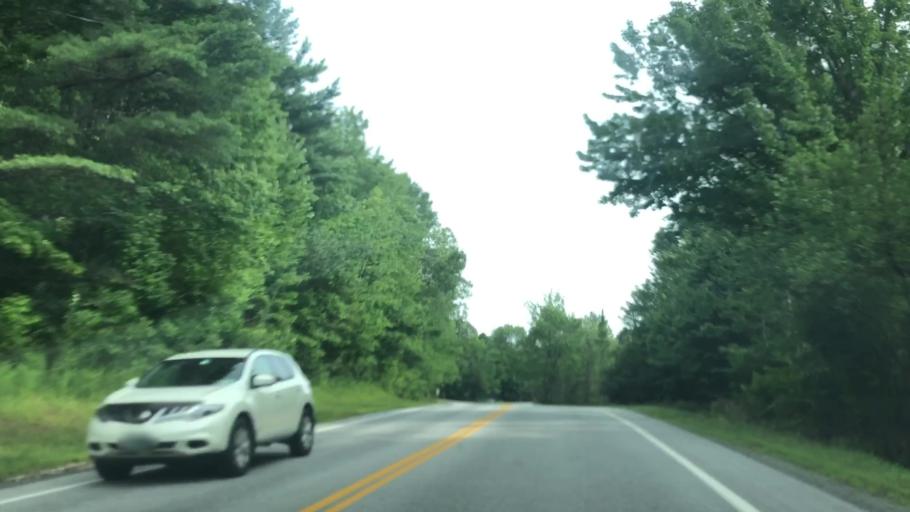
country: US
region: Vermont
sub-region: Rutland County
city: Rutland
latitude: 43.6815
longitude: -72.8124
